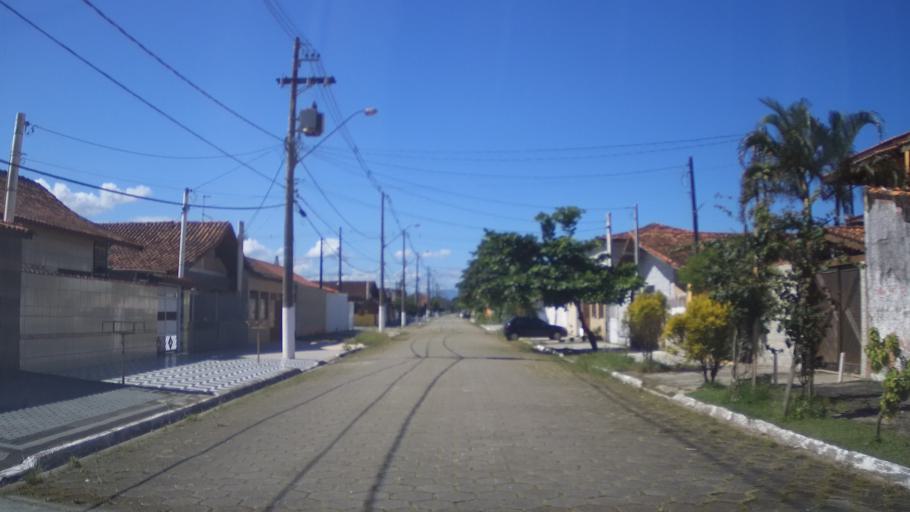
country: BR
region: Sao Paulo
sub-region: Praia Grande
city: Praia Grande
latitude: -24.0399
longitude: -46.5026
